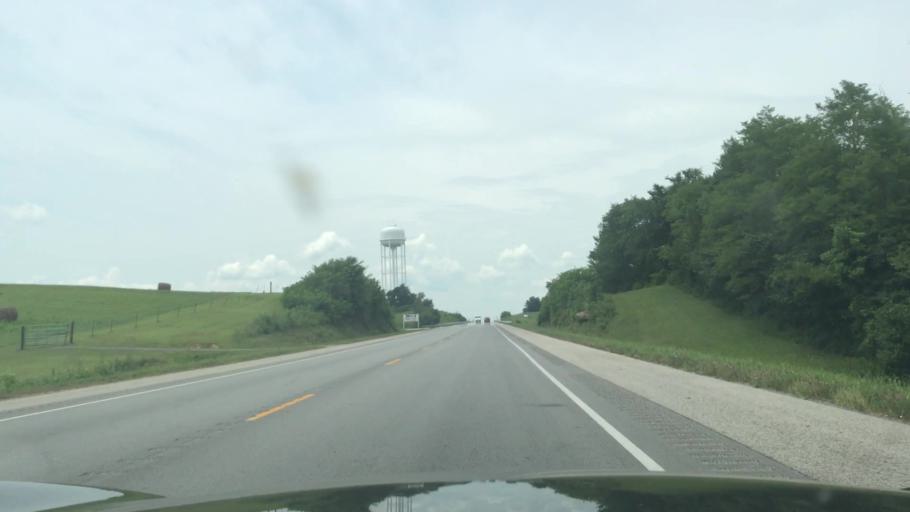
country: US
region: Kentucky
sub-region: Green County
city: Greensburg
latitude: 37.3104
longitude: -85.4290
